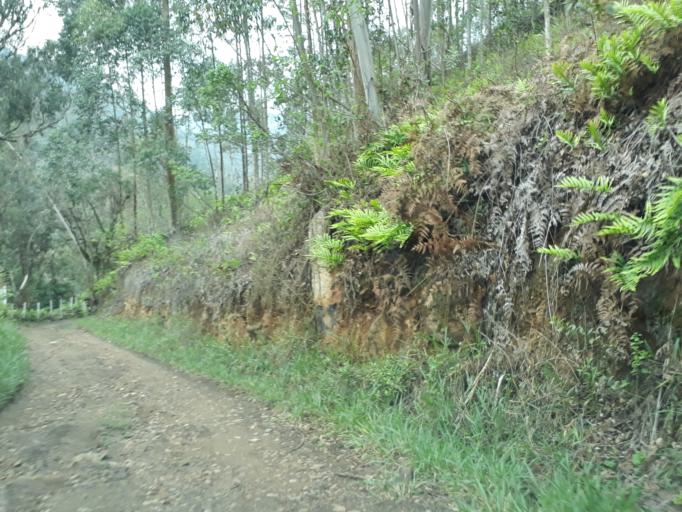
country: CO
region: Cundinamarca
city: Manta
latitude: 5.0611
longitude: -73.5258
